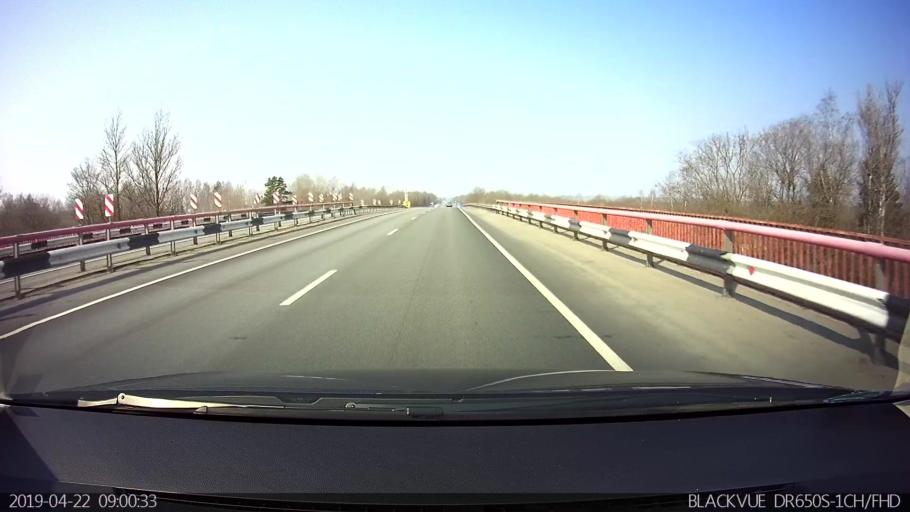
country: RU
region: Smolensk
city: Pechersk
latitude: 54.8623
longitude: 31.9412
